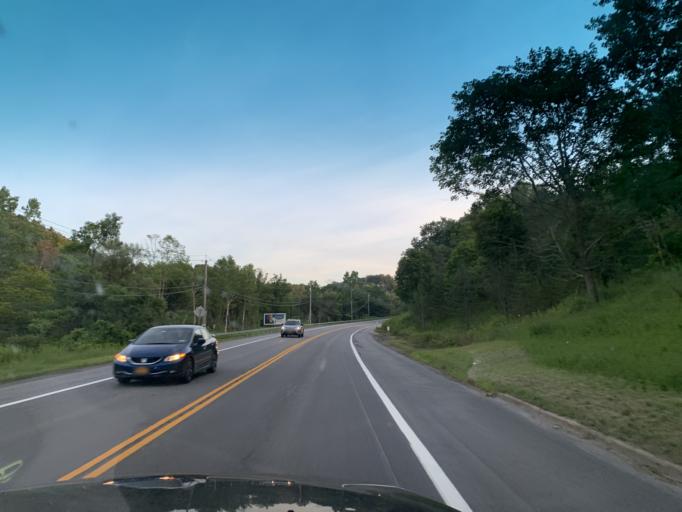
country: US
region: New York
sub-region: Oneida County
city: Chadwicks
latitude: 42.9488
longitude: -75.2447
